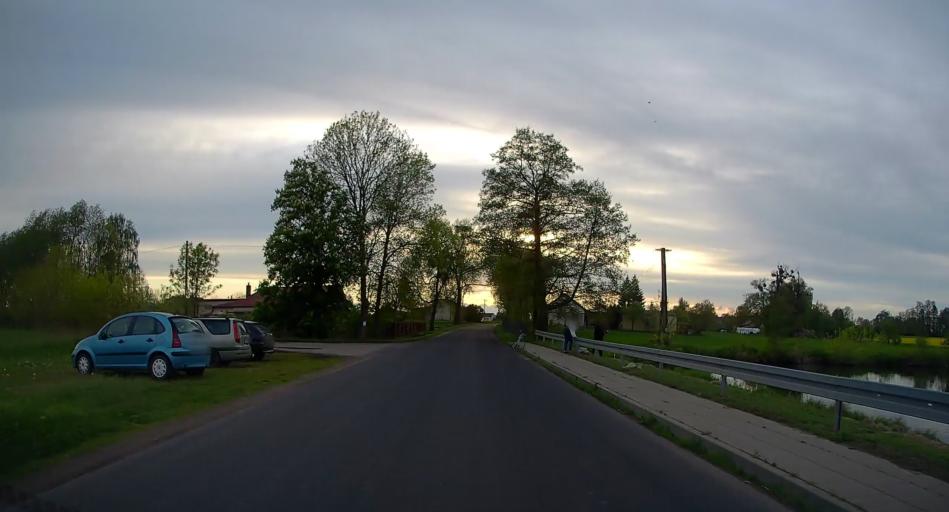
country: PL
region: Masovian Voivodeship
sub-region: Powiat plocki
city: Mala Wies
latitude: 52.4544
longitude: 20.0943
